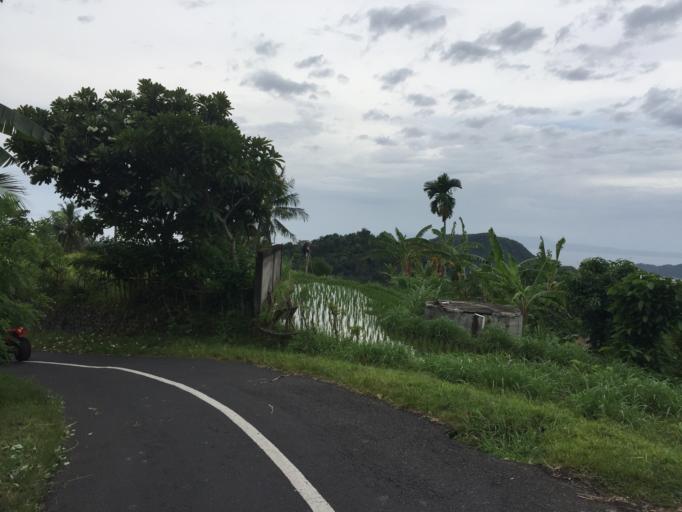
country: ID
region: Bali
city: Banjar Kawan
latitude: -8.4737
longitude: 115.5189
